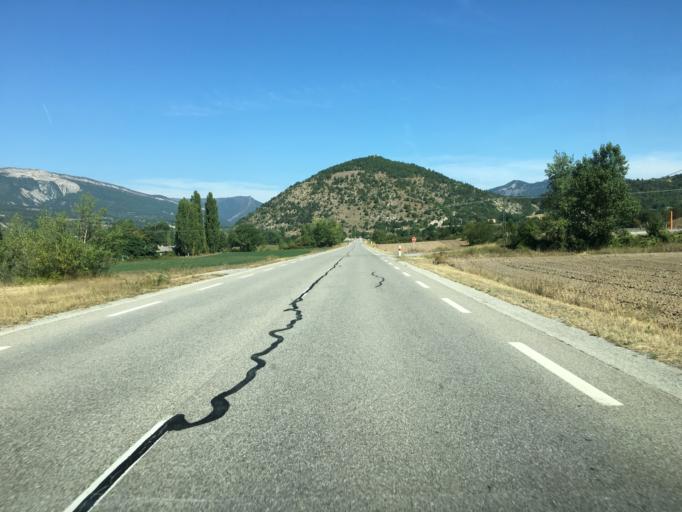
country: FR
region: Provence-Alpes-Cote d'Azur
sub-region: Departement des Hautes-Alpes
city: Serres
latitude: 44.3700
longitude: 5.7538
